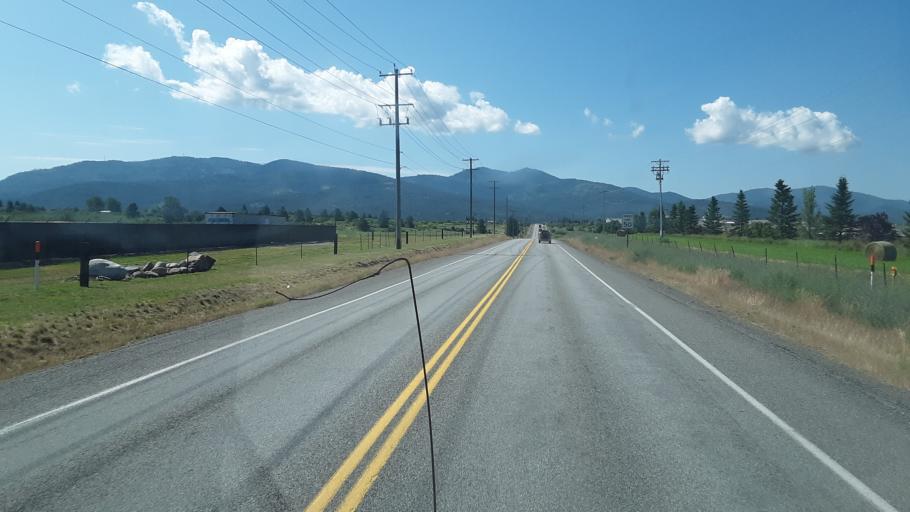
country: US
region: Idaho
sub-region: Kootenai County
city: Post Falls
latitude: 47.7308
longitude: -117.0018
